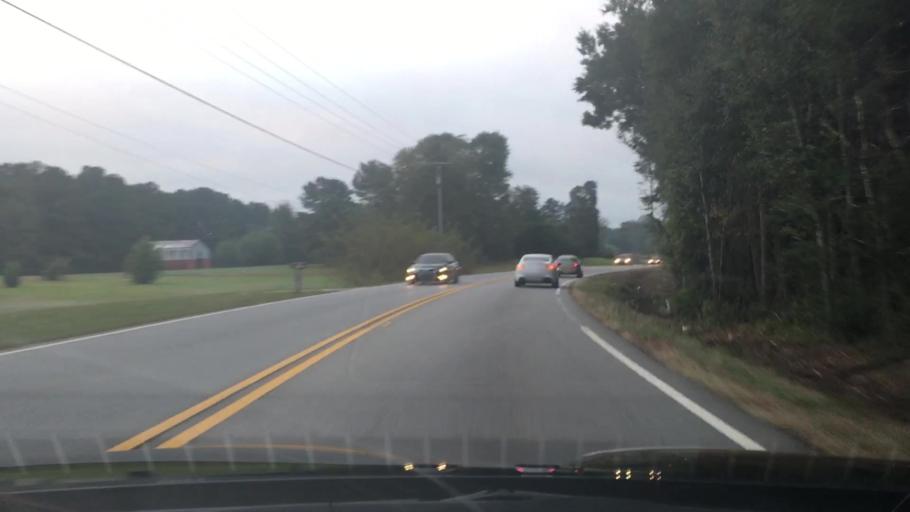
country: US
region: Georgia
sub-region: Fayette County
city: Peachtree City
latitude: 33.3695
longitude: -84.6633
